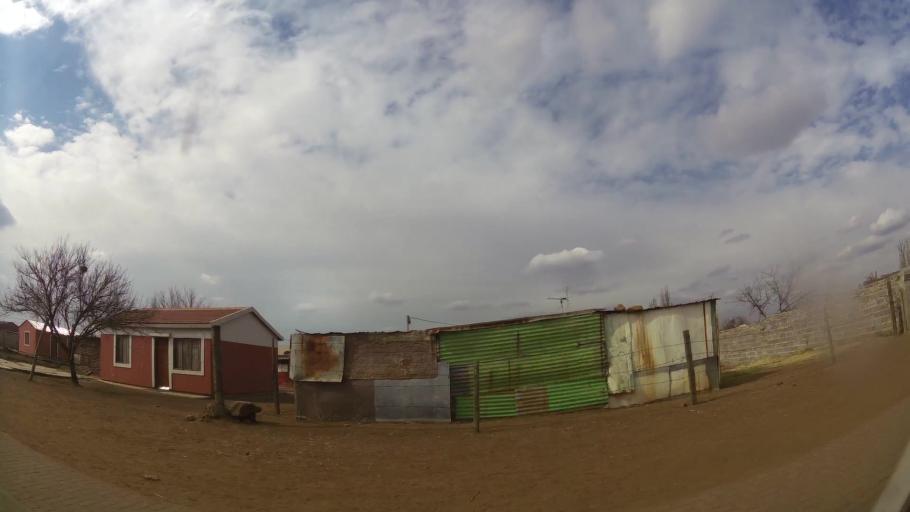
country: ZA
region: Gauteng
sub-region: Ekurhuleni Metropolitan Municipality
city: Germiston
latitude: -26.4025
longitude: 28.1635
